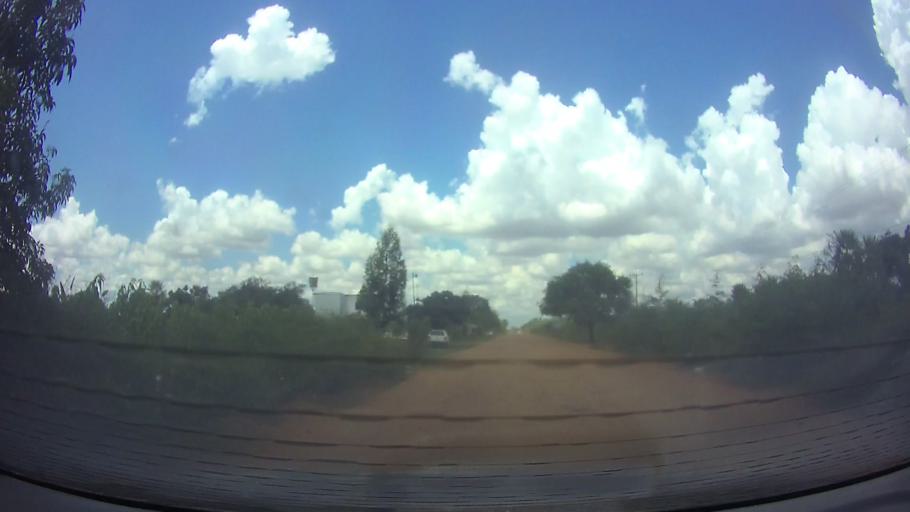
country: PY
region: Presidente Hayes
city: Nanawa
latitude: -25.2498
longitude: -57.6492
